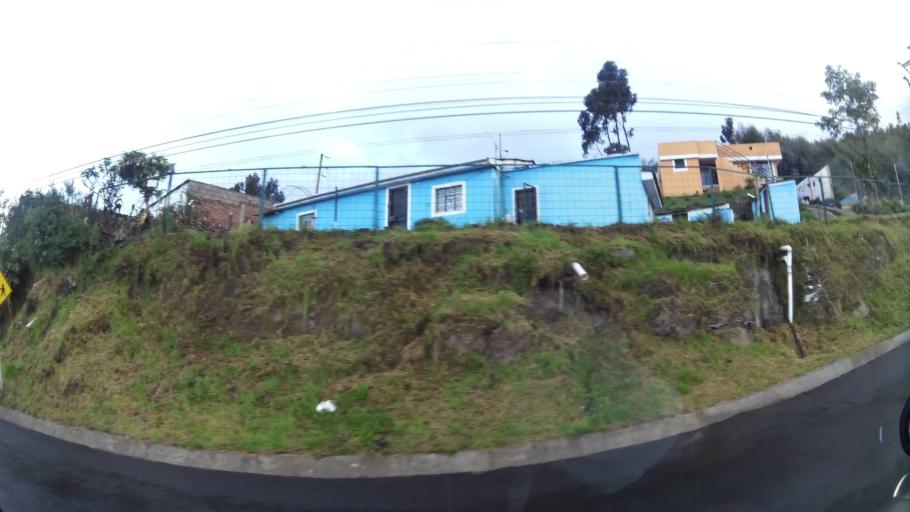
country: EC
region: Pichincha
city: Quito
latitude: -0.1098
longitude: -78.5185
